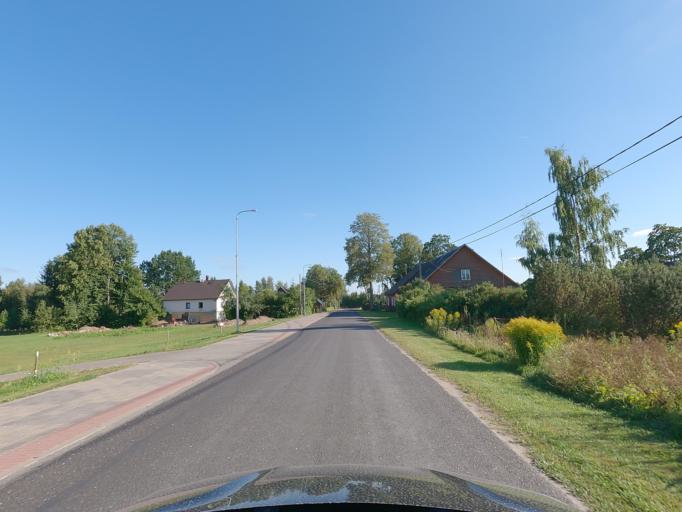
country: EE
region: Raplamaa
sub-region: Rapla vald
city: Rapla
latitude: 59.0119
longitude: 24.7859
